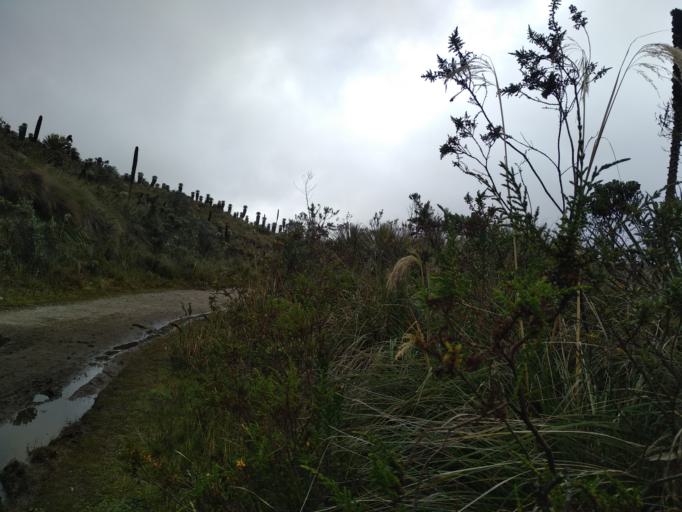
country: EC
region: Carchi
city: San Gabriel
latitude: 0.6889
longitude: -77.8495
